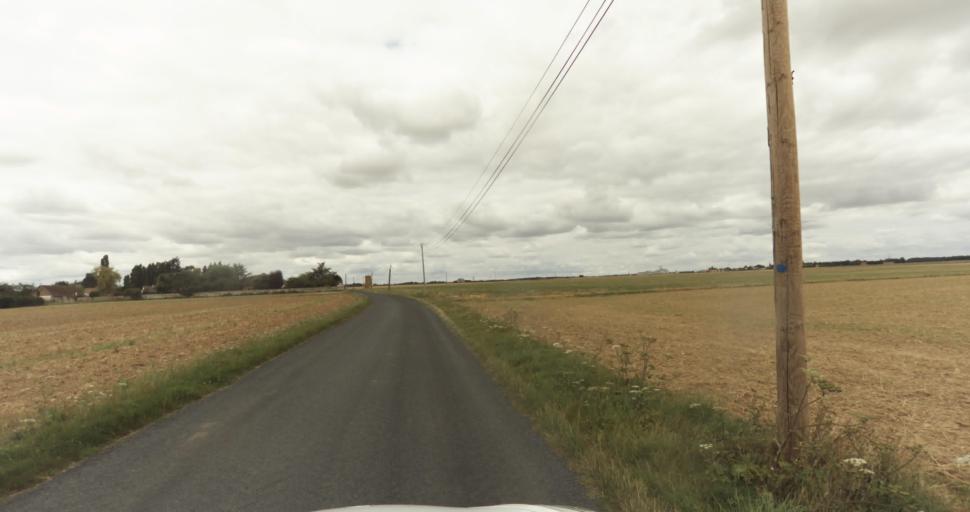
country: FR
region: Haute-Normandie
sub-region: Departement de l'Eure
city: La Madeleine-de-Nonancourt
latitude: 48.8223
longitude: 1.2121
